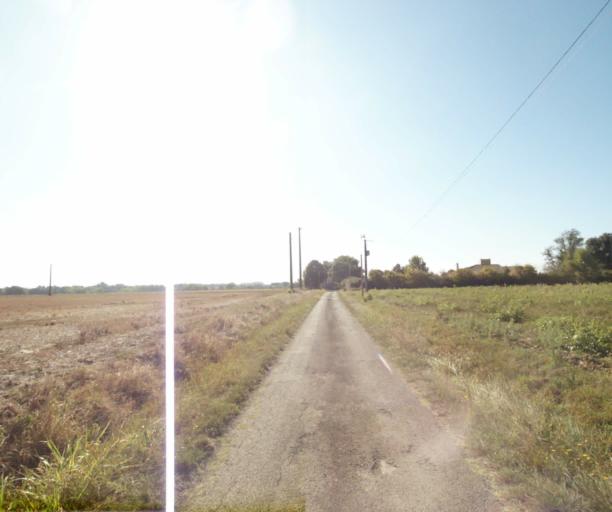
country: FR
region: Midi-Pyrenees
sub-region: Departement du Tarn-et-Garonne
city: Verdun-sur-Garonne
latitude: 43.8674
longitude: 1.2164
